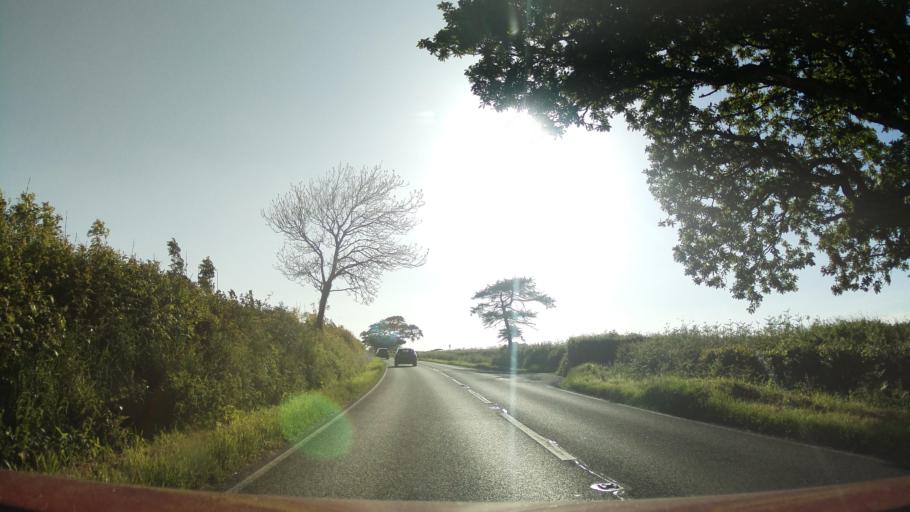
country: GB
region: England
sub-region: Devon
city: Colyton
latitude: 50.7183
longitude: -3.0931
